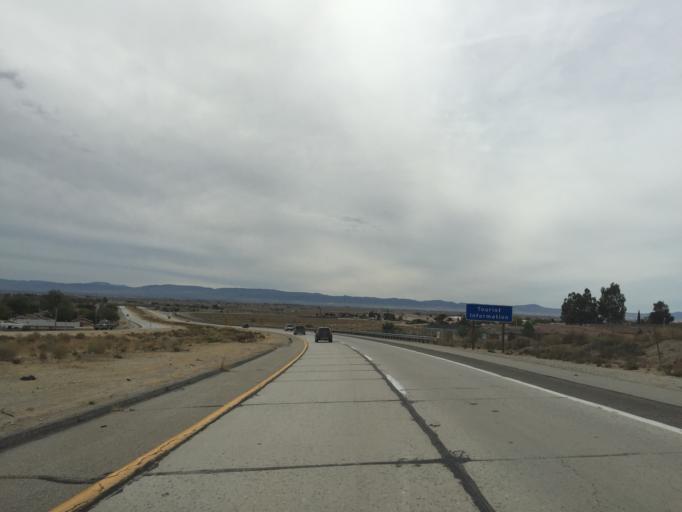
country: US
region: California
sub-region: Kern County
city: Rosamond
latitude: 34.8735
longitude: -118.1710
